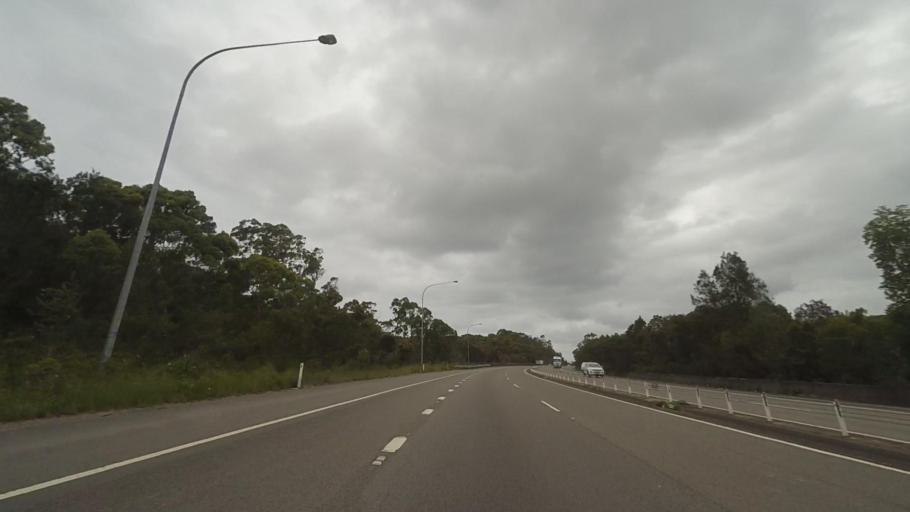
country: AU
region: New South Wales
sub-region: Lake Macquarie Shire
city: Arcadia vale
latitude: -33.1147
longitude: 151.6279
